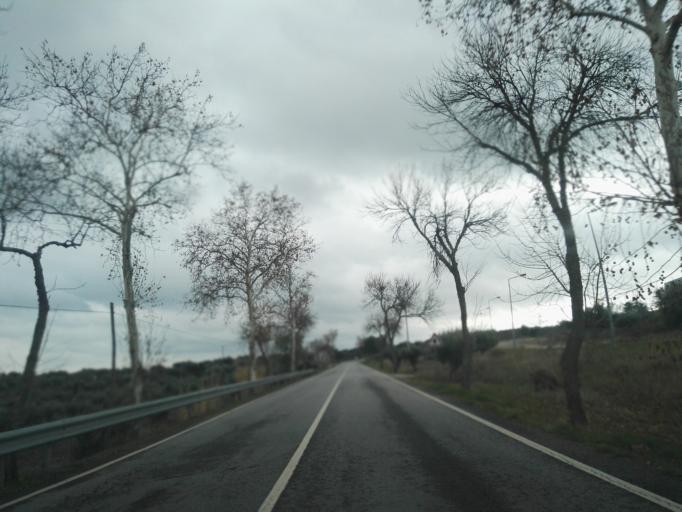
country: PT
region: Portalegre
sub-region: Arronches
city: Arronches
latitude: 39.1141
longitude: -7.2860
